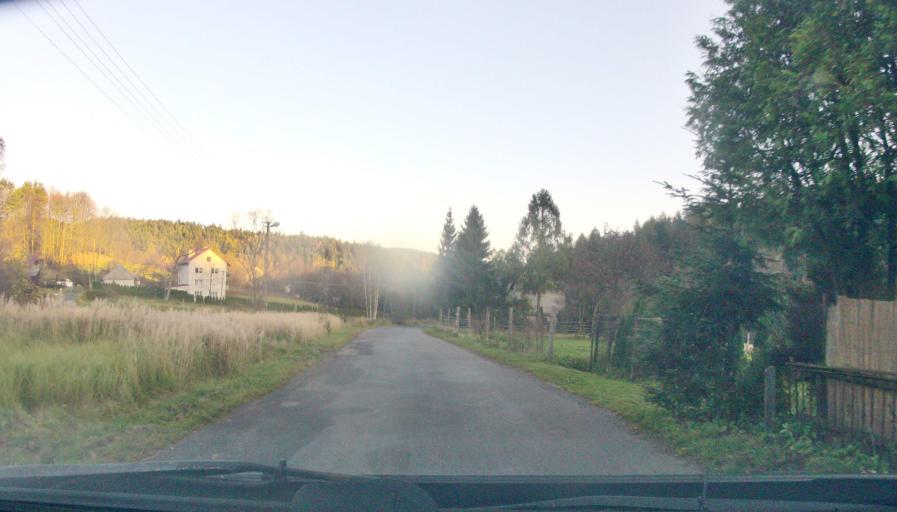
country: PL
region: Lesser Poland Voivodeship
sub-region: Powiat suski
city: Krzeszow
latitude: 49.7626
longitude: 19.4521
